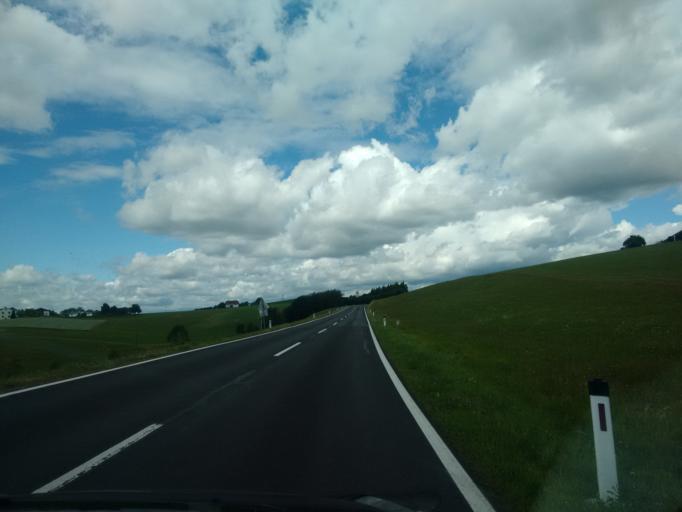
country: AT
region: Upper Austria
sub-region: Politischer Bezirk Urfahr-Umgebung
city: Gramastetten
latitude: 48.4088
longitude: 14.1708
